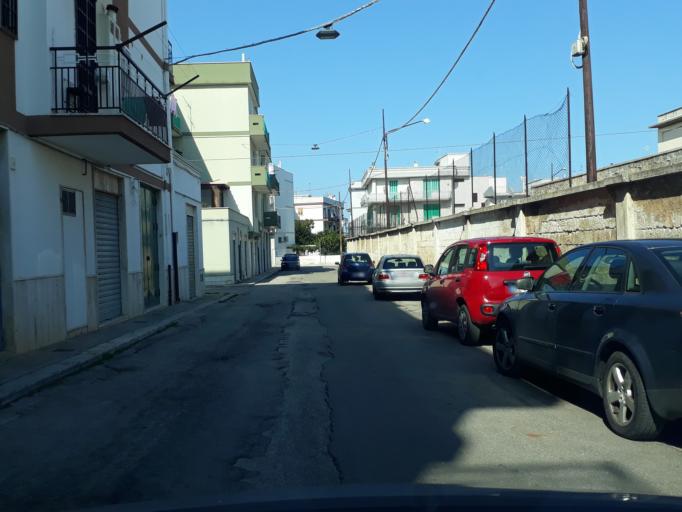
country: IT
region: Apulia
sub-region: Provincia di Brindisi
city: Fasano
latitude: 40.8388
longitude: 17.3620
